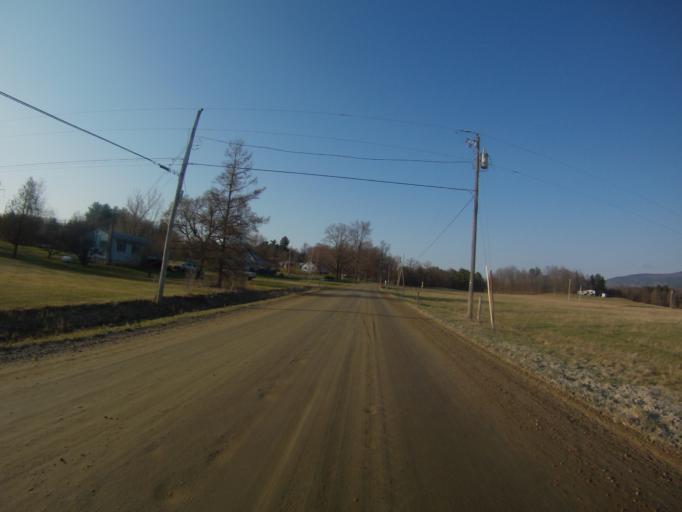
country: US
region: Vermont
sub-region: Addison County
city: Middlebury (village)
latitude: 44.0484
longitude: -73.1463
